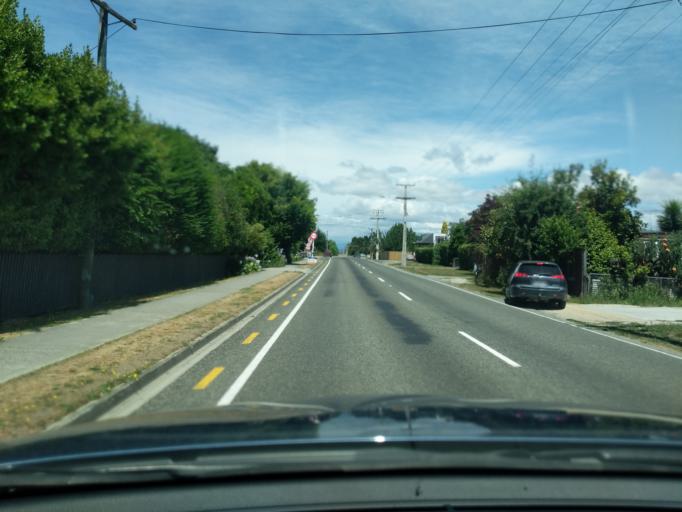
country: NZ
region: Tasman
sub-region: Tasman District
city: Motueka
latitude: -41.0791
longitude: 172.9973
